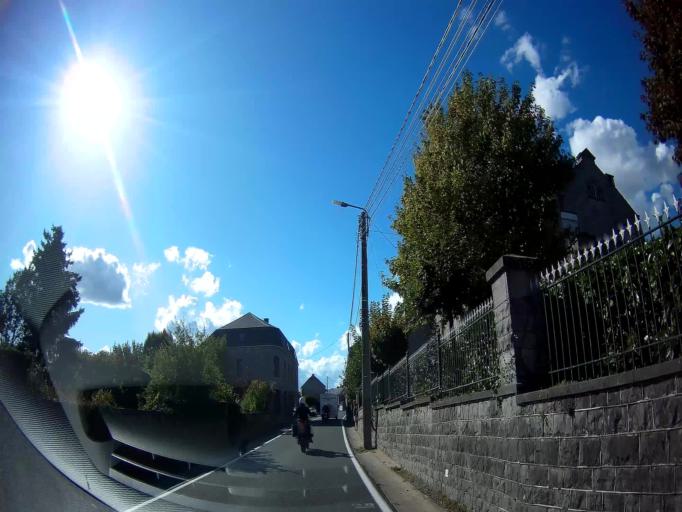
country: BE
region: Wallonia
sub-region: Province de Namur
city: Mettet
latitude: 50.3182
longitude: 4.7517
